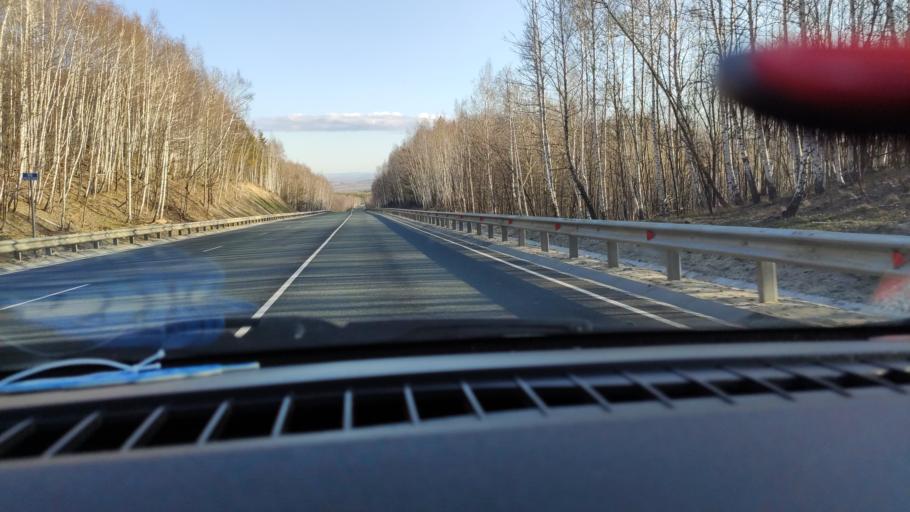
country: RU
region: Saratov
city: Khvalynsk
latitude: 52.5021
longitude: 48.0151
